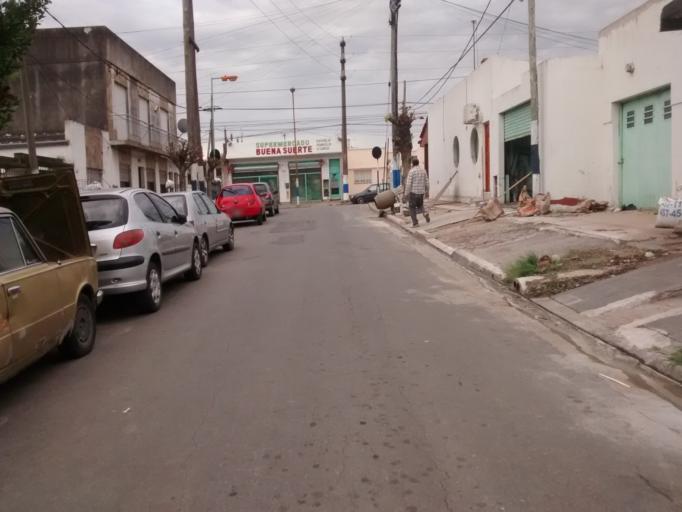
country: AR
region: Buenos Aires
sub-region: Partido de La Plata
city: La Plata
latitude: -34.9389
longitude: -57.9208
